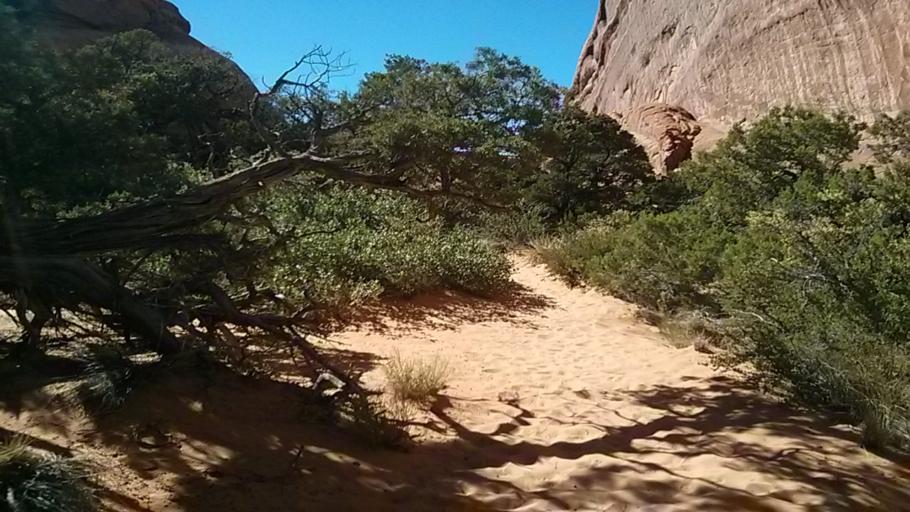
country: US
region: Utah
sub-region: Grand County
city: Moab
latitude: 38.8019
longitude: -109.6150
